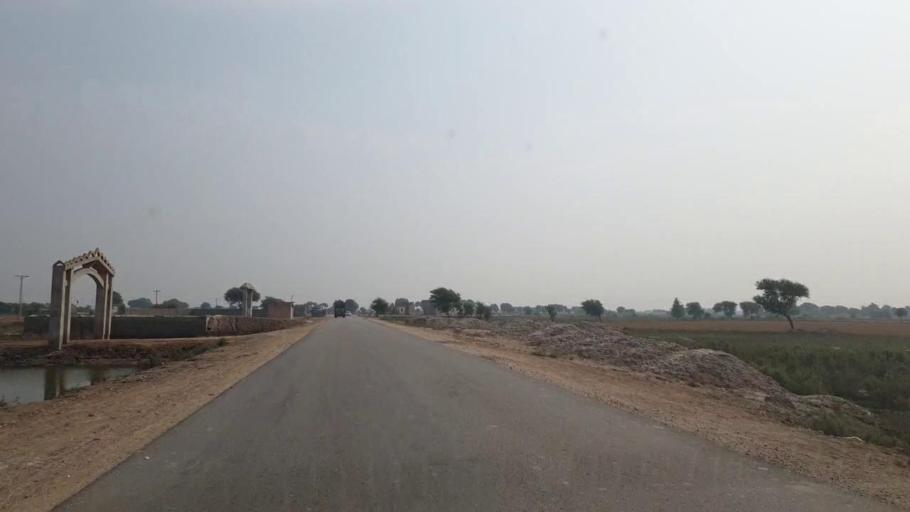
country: PK
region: Sindh
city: Matli
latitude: 25.0543
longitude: 68.6773
